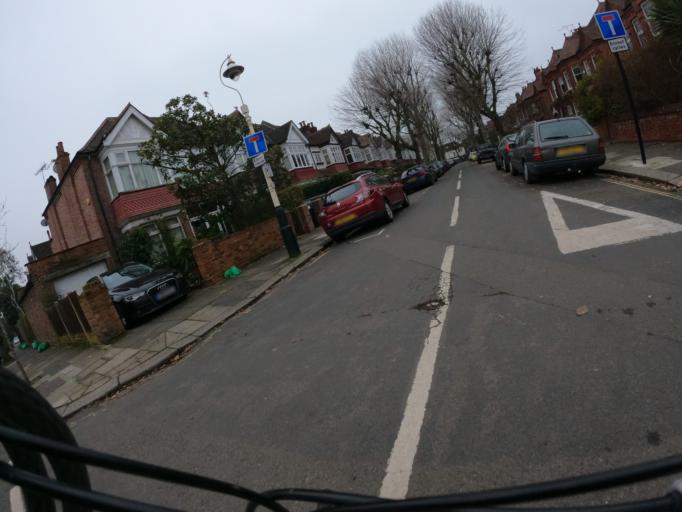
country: GB
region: England
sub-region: Greater London
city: Ealing
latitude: 51.5072
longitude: -0.3133
